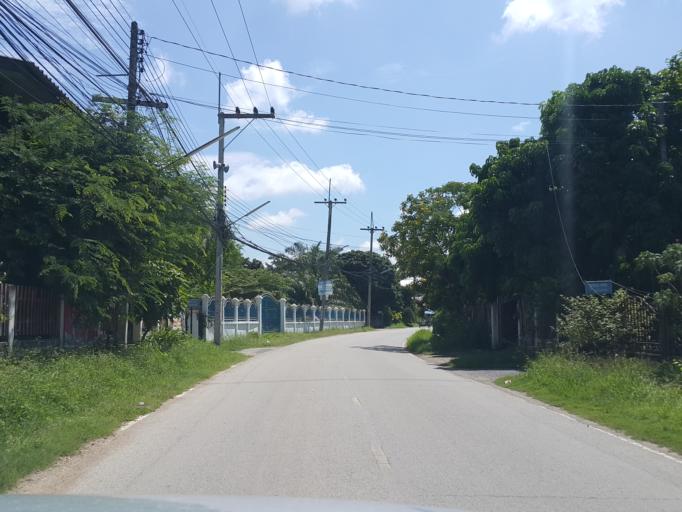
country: TH
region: Chiang Mai
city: San Kamphaeng
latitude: 18.7209
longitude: 99.1029
